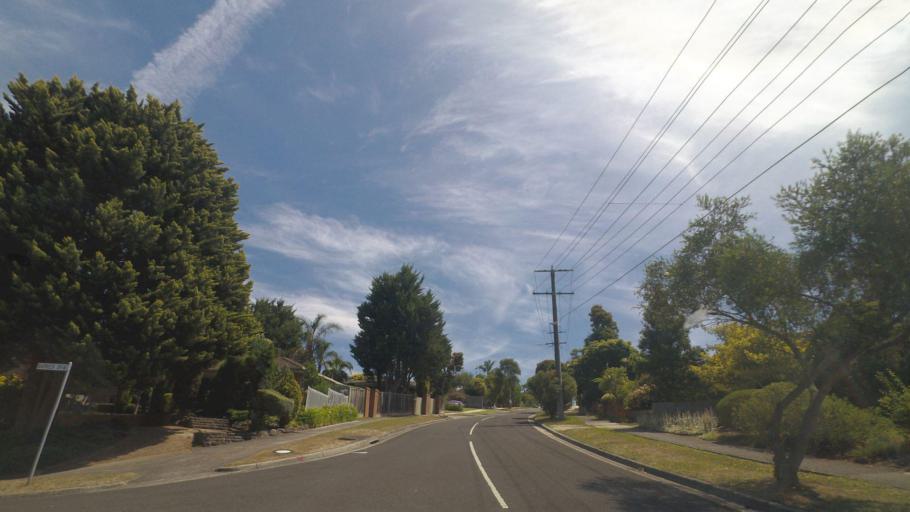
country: AU
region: Victoria
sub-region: Maroondah
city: Croydon North
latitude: -37.7691
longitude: 145.3090
